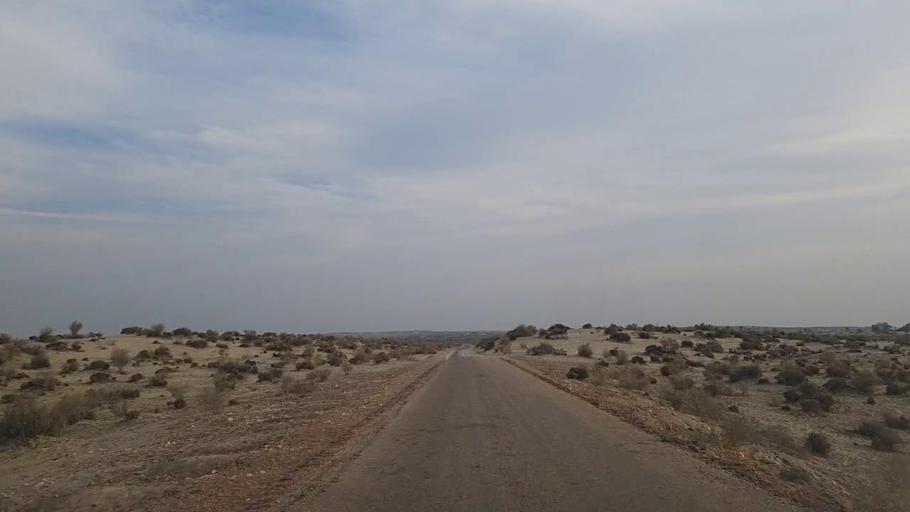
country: PK
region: Sindh
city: Daur
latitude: 26.5011
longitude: 68.5203
